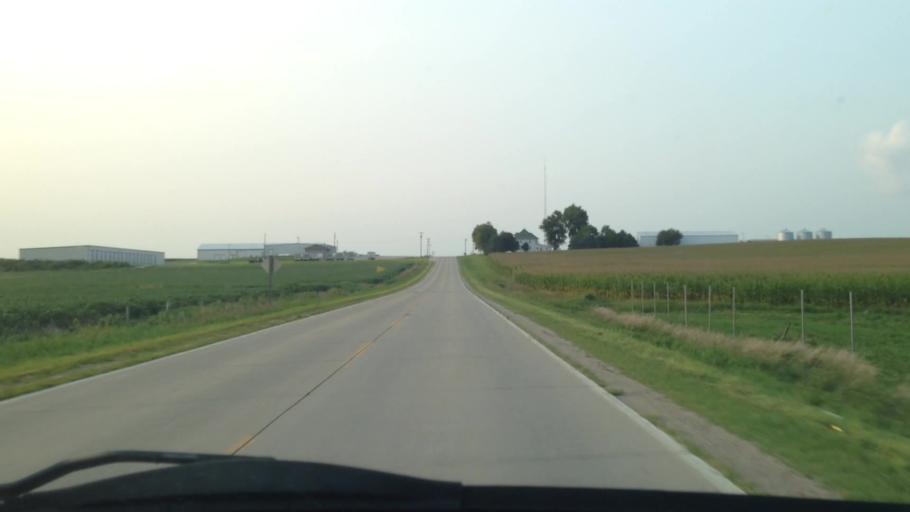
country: US
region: Iowa
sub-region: Benton County
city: Atkins
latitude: 41.9657
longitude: -91.8727
